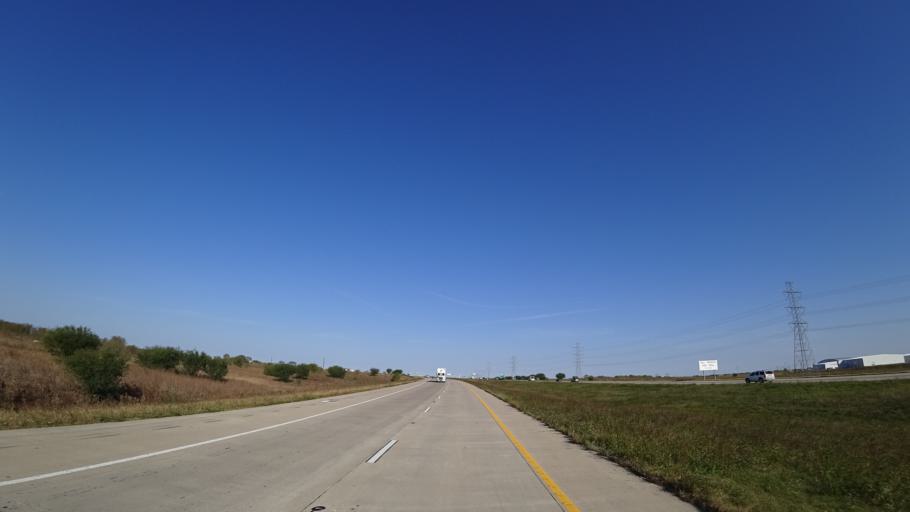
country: US
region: Texas
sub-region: Travis County
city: Manor
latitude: 30.3934
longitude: -97.5795
